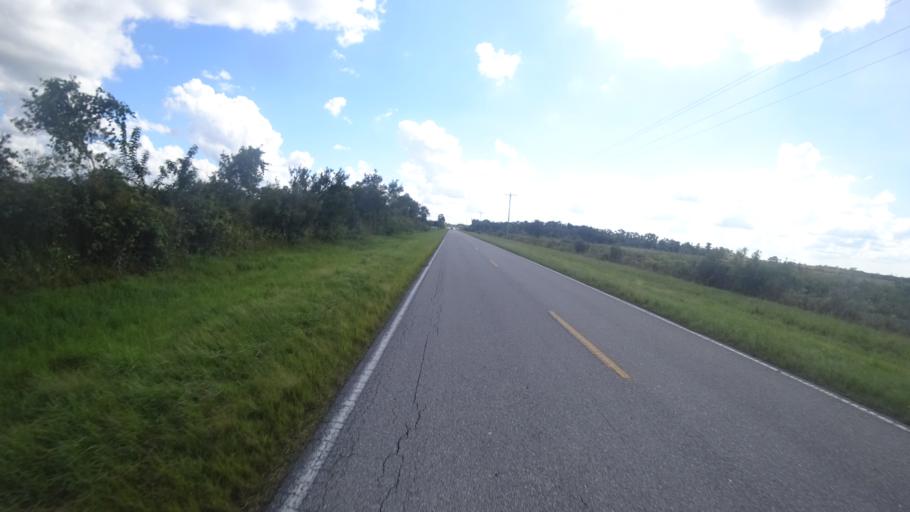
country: US
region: Florida
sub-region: Sarasota County
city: Lake Sarasota
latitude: 27.4178
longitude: -82.1332
